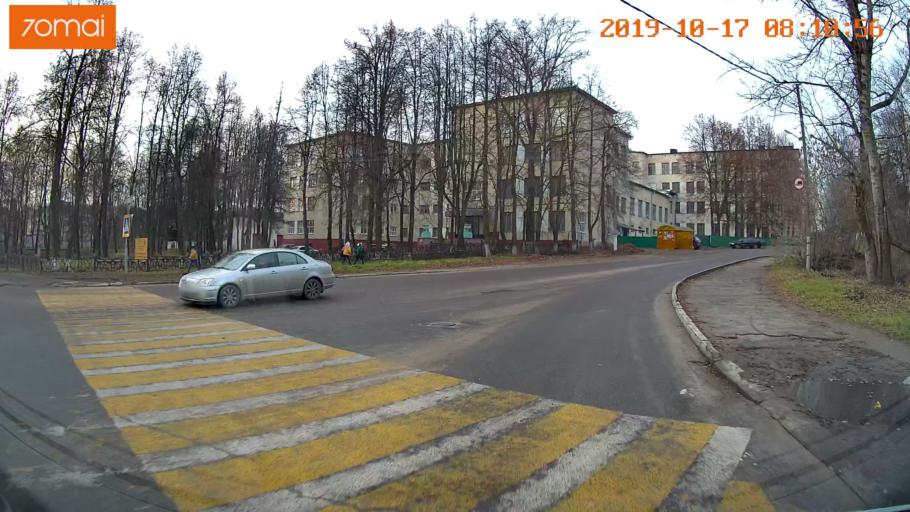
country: RU
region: Vladimir
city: Kol'chugino
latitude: 56.3047
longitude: 39.3762
